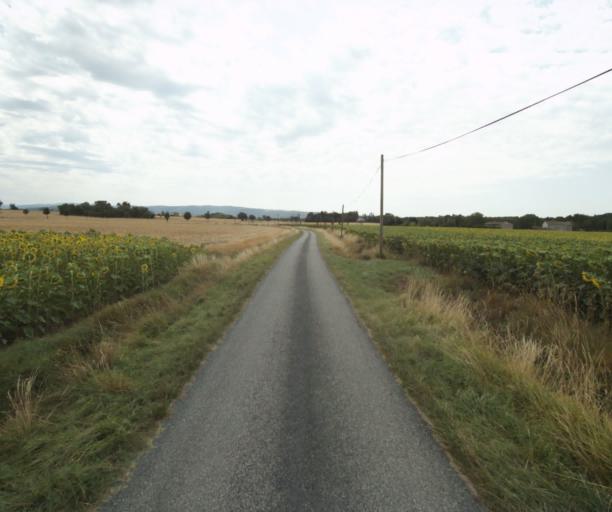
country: FR
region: Midi-Pyrenees
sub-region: Departement de la Haute-Garonne
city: Saint-Felix-Lauragais
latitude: 43.4357
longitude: 1.9195
